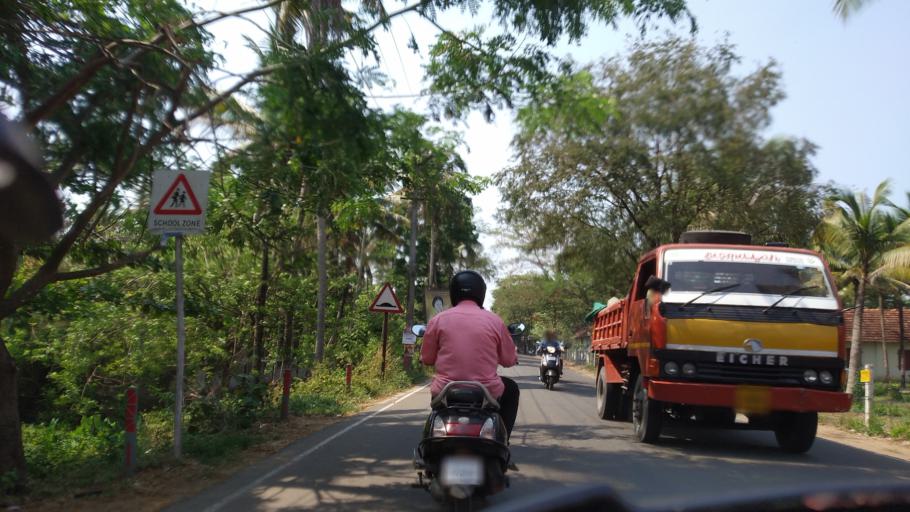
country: IN
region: Kerala
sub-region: Thrissur District
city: Kodungallur
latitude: 10.2212
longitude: 76.1584
